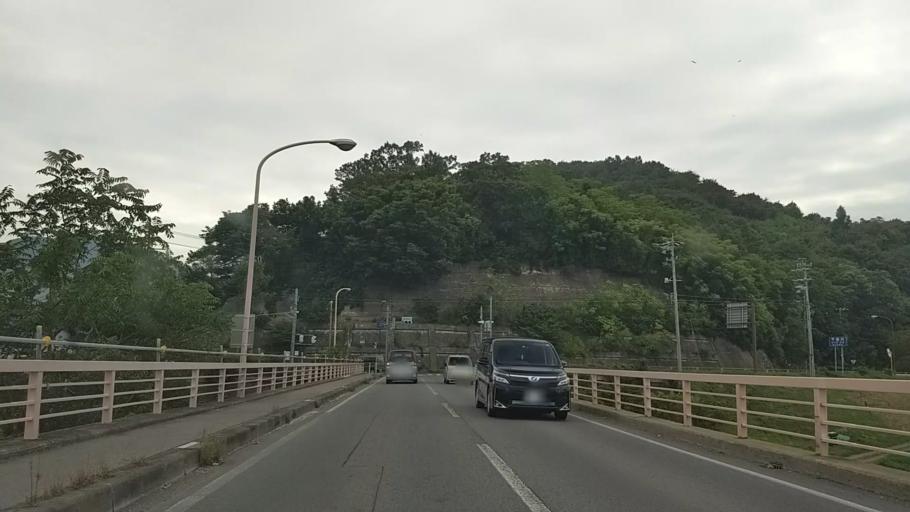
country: JP
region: Nagano
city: Nagano-shi
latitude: 36.6053
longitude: 138.2251
